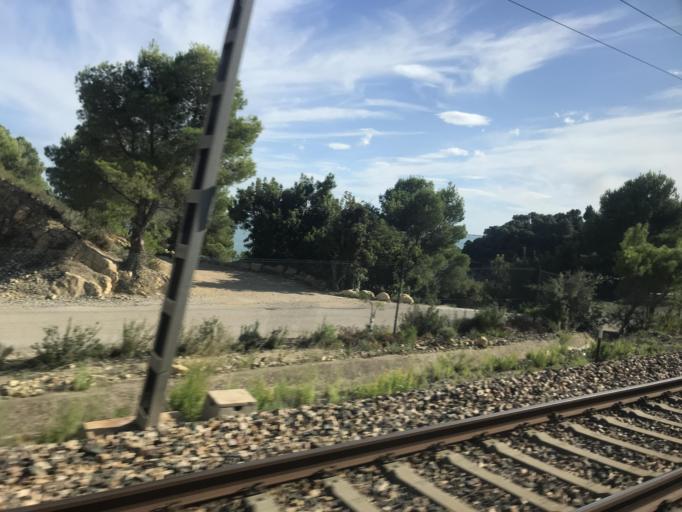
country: ES
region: Catalonia
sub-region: Provincia de Tarragona
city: El Perello
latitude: 40.8449
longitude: 0.7492
